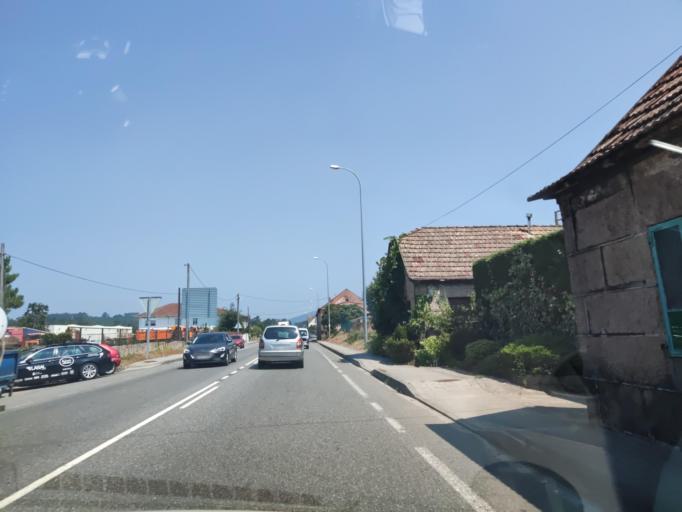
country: ES
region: Galicia
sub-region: Provincia de Pontevedra
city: Porrino
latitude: 42.1719
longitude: -8.6185
